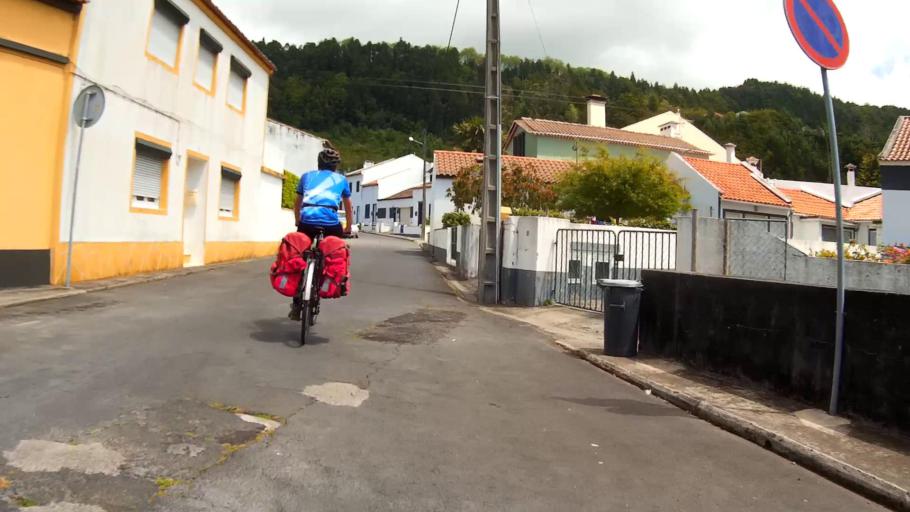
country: PT
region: Azores
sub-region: Povoacao
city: Furnas
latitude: 37.7761
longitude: -25.3124
